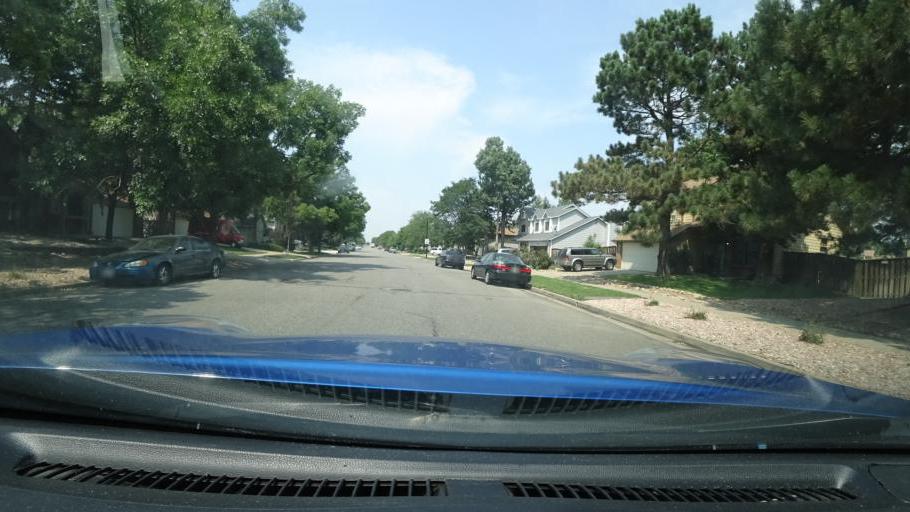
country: US
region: Colorado
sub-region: Adams County
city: Aurora
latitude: 39.7779
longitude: -104.7654
